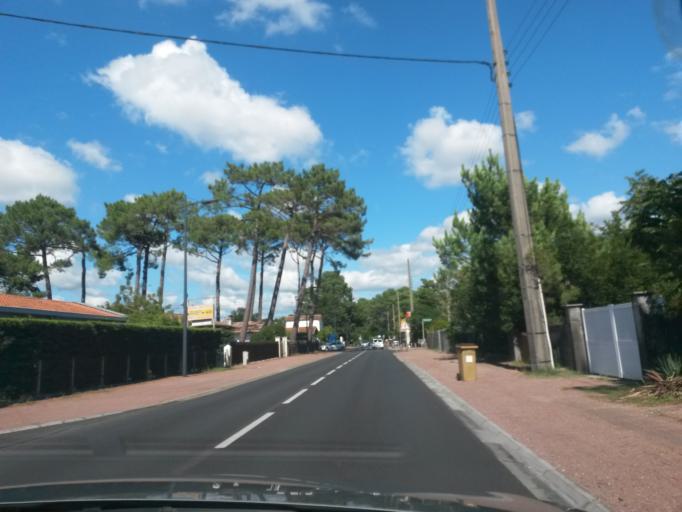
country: FR
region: Aquitaine
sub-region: Departement de la Gironde
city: Ares
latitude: 44.7270
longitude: -1.1987
